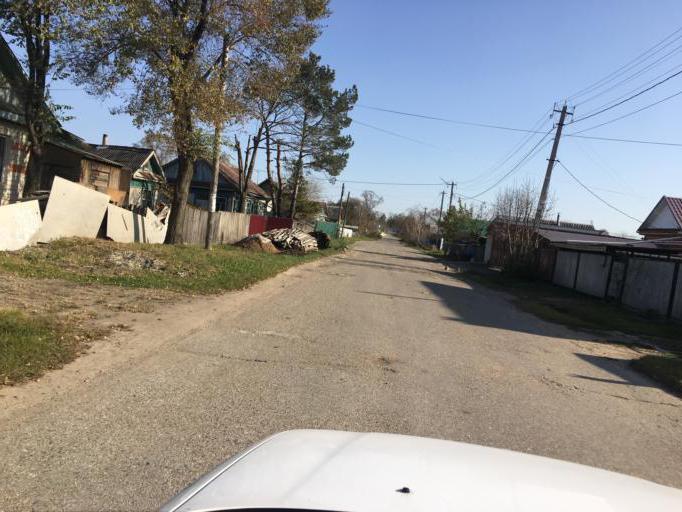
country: RU
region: Primorskiy
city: Dal'nerechensk
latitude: 45.9251
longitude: 133.7232
